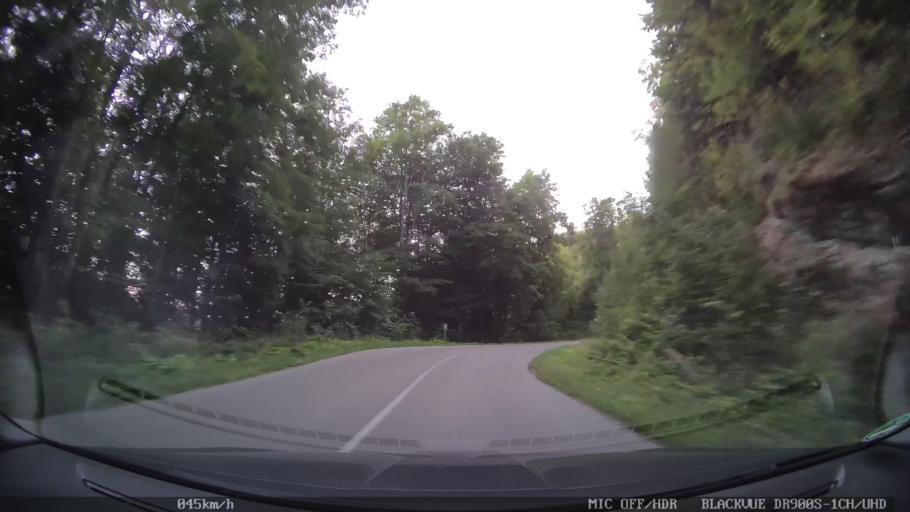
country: HR
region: Primorsko-Goranska
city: Vrbovsko
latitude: 45.2025
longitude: 15.0263
